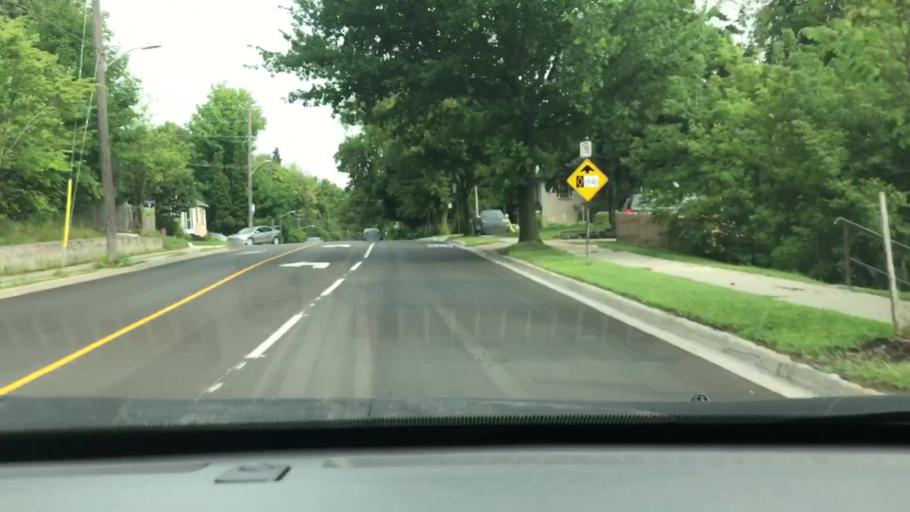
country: CA
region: Ontario
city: Newmarket
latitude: 44.0615
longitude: -79.4622
